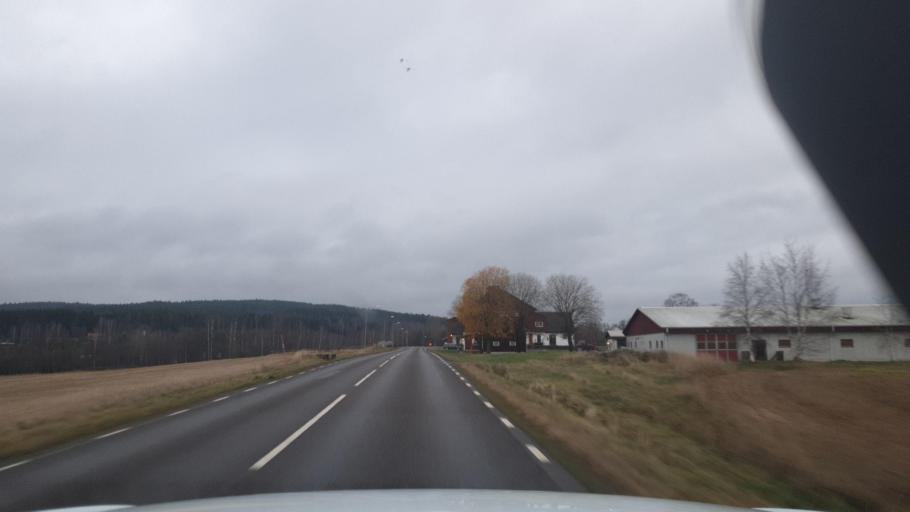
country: SE
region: Vaermland
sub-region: Arvika Kommun
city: Arvika
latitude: 59.7555
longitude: 12.5471
